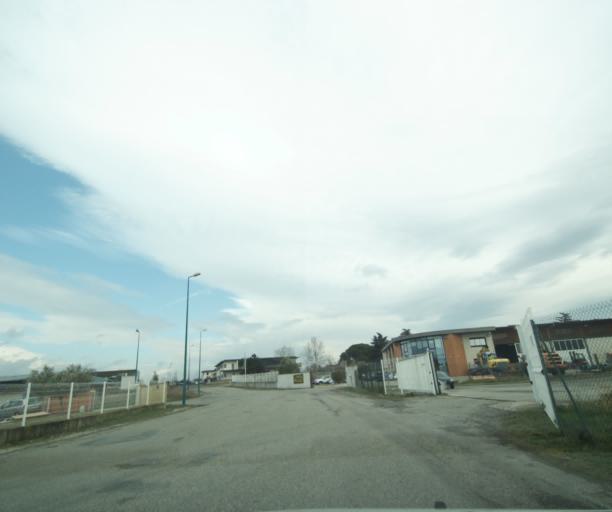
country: FR
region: Rhone-Alpes
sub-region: Departement de l'Ardeche
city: Cornas
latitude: 44.9680
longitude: 4.8778
